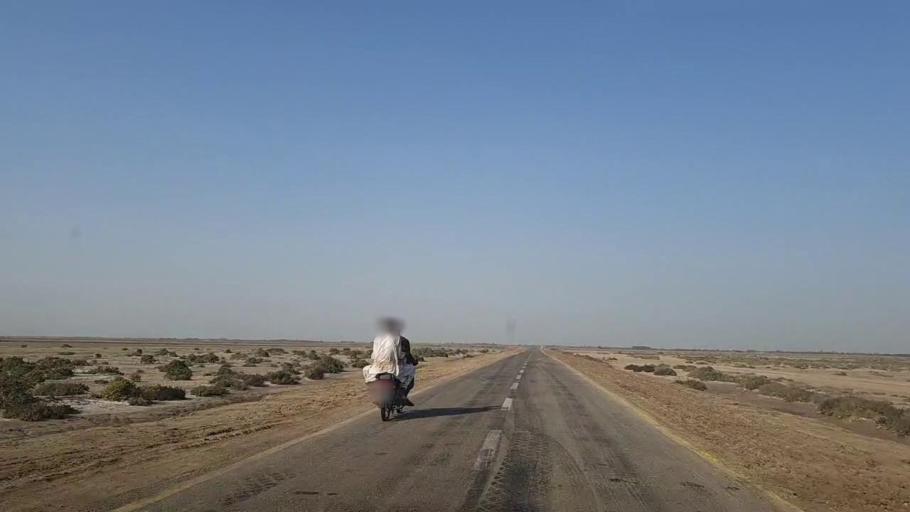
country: PK
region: Sindh
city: Jati
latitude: 24.4912
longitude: 68.3754
